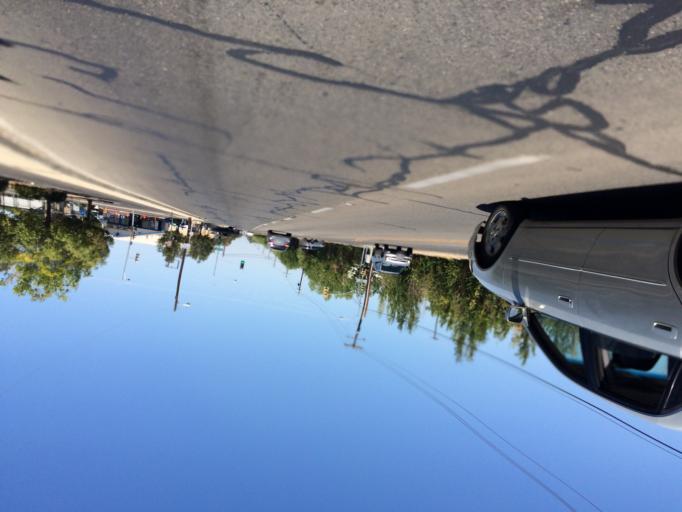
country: US
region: California
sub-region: Fresno County
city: Fresno
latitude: 36.7277
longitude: -119.7456
